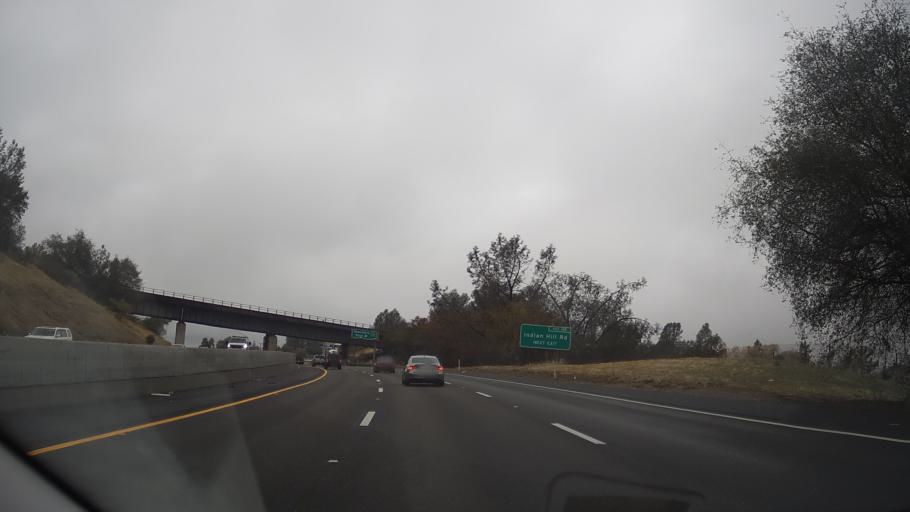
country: US
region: California
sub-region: Placer County
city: Newcastle
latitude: 38.8769
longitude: -121.1296
